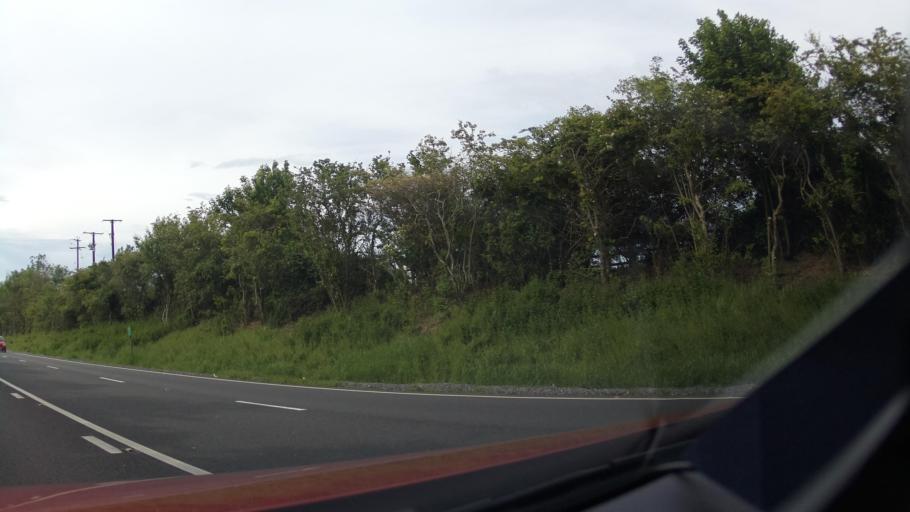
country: GB
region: England
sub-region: Northumberland
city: Berwick-Upon-Tweed
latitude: 55.7532
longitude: -2.0357
